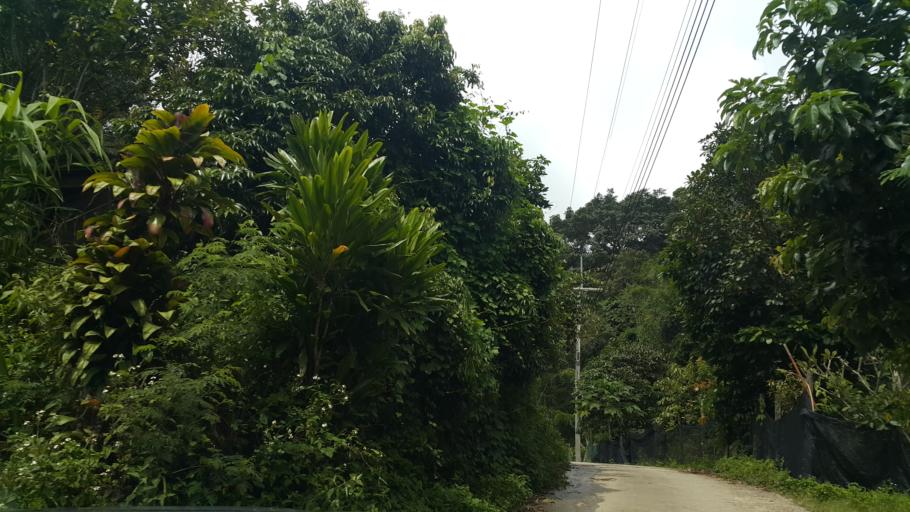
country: TH
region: Lampang
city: Wang Nuea
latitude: 19.0903
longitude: 99.3719
